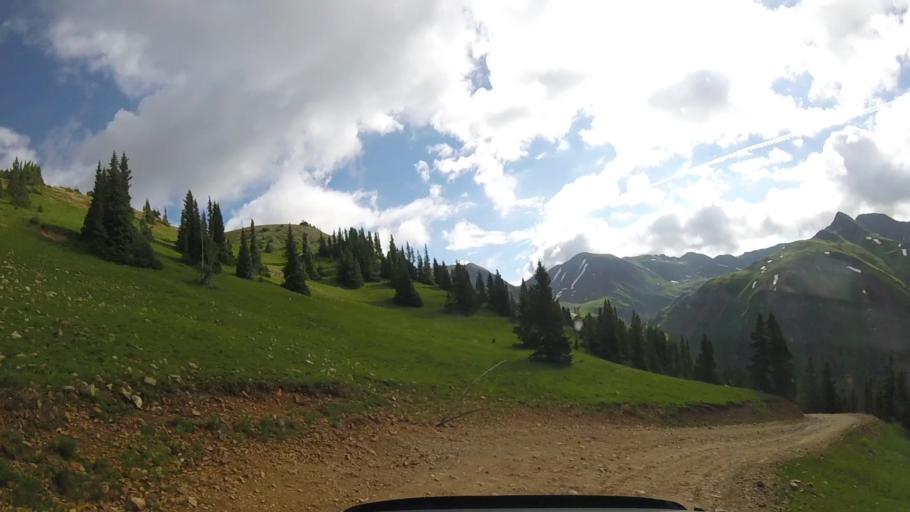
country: US
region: Colorado
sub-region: San Juan County
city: Silverton
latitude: 37.9068
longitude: -107.6547
